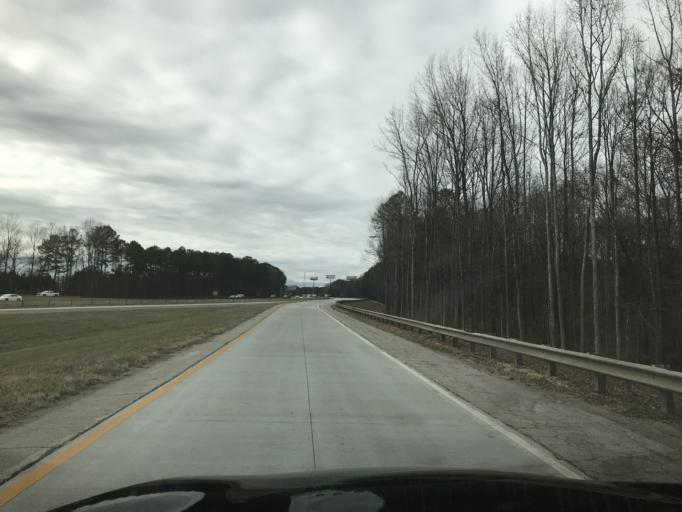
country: US
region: Georgia
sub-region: Carroll County
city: Villa Rica
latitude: 33.7258
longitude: -84.9025
